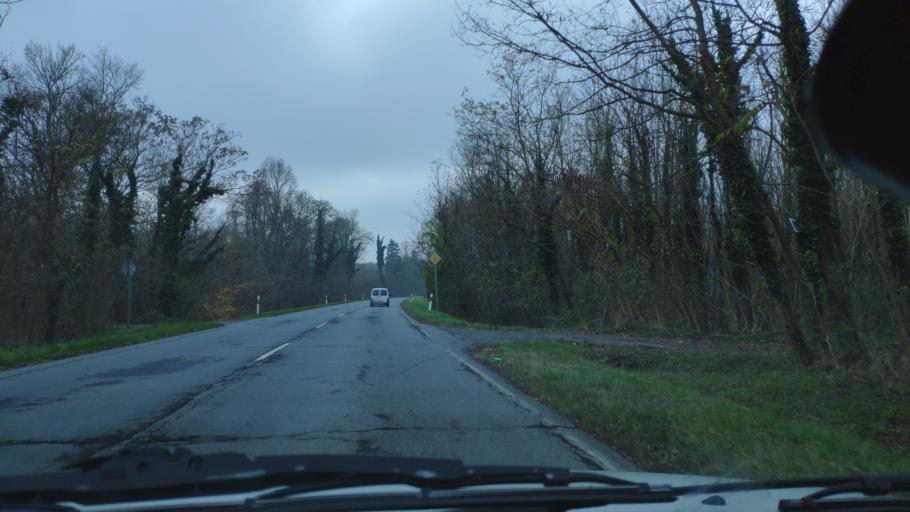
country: HU
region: Zala
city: Zalakomar
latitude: 46.5399
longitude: 17.2439
